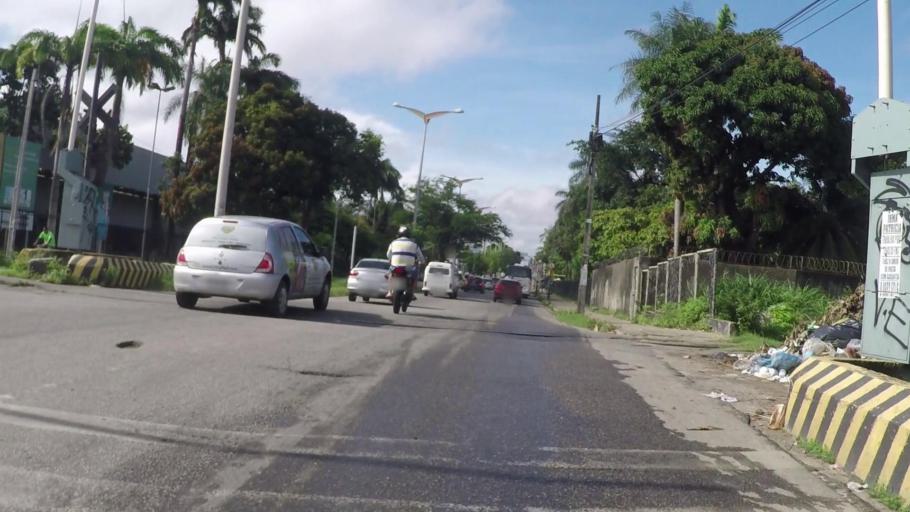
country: BR
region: Ceara
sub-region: Fortaleza
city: Fortaleza
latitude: -3.7316
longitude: -38.5847
